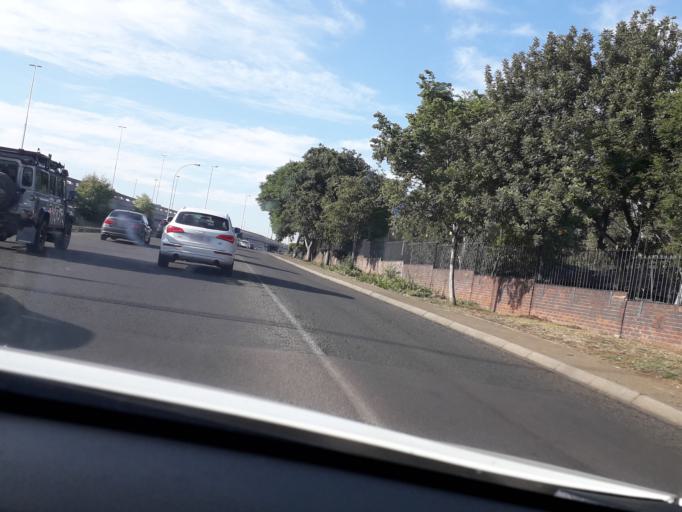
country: ZA
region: Gauteng
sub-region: City of Johannesburg Metropolitan Municipality
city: Modderfontein
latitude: -26.1636
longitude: 28.1329
